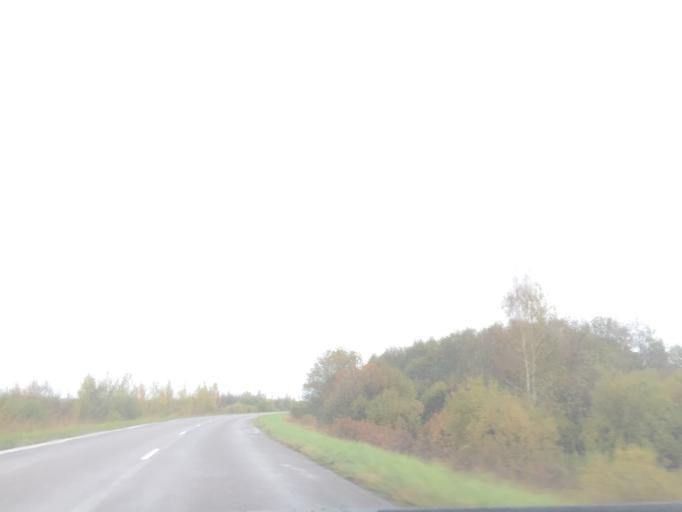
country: LV
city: Tireli
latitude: 56.8131
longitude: 23.5732
